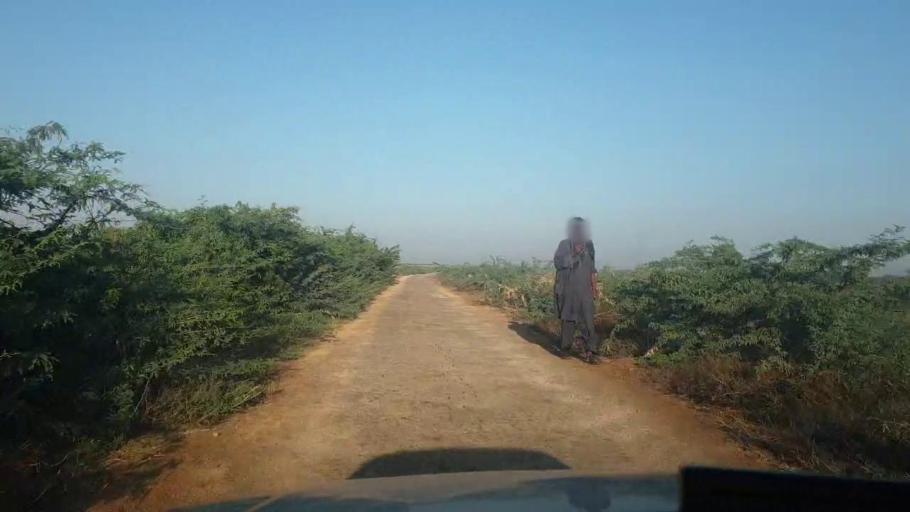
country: PK
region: Sindh
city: Thatta
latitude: 24.7015
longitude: 67.8521
